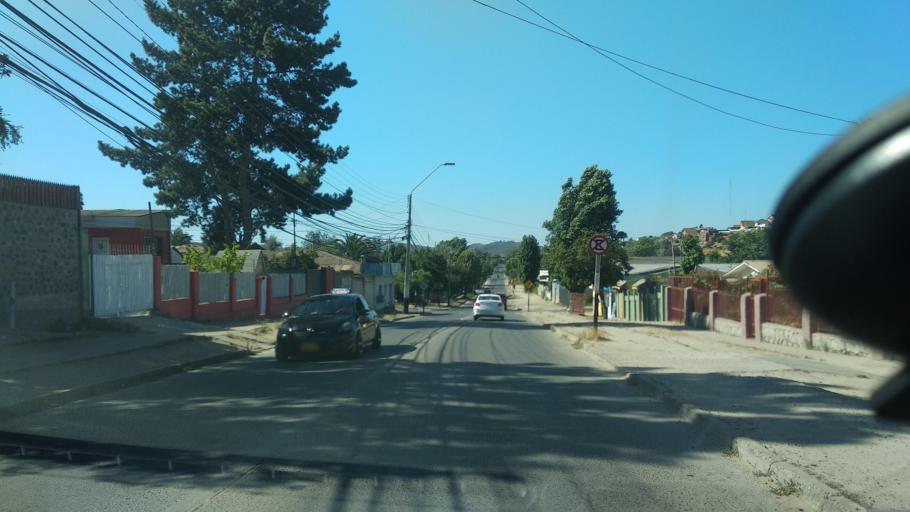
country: CL
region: Valparaiso
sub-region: Provincia de Marga Marga
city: Villa Alemana
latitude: -33.0558
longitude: -71.3735
